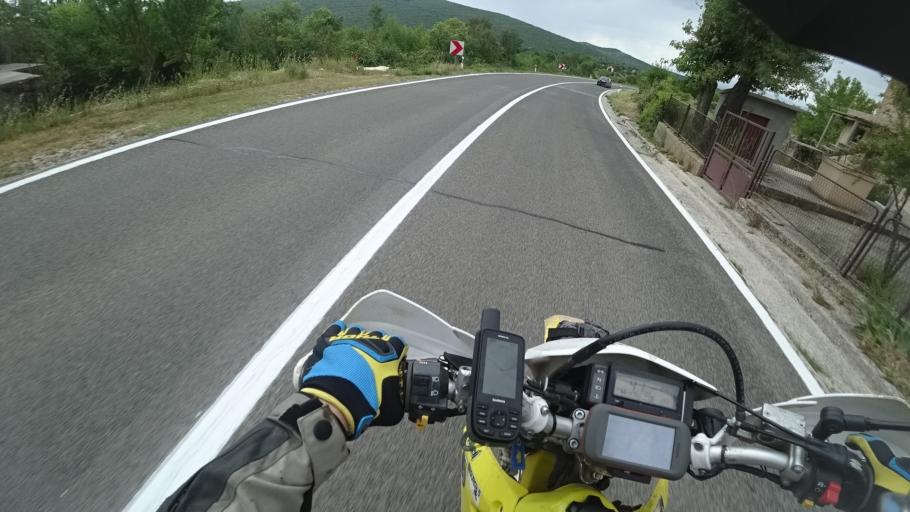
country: HR
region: Sibensko-Kniniska
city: Knin
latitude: 43.9917
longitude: 16.3053
